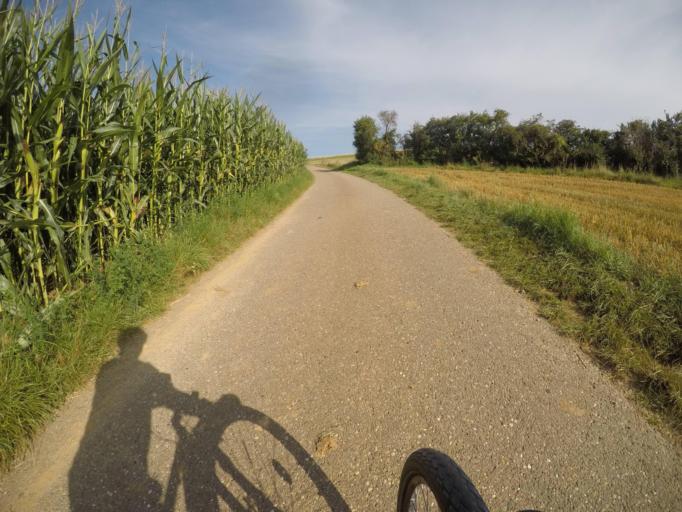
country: DE
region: Baden-Wuerttemberg
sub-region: Regierungsbezirk Stuttgart
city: Weissach
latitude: 48.8375
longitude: 8.9414
